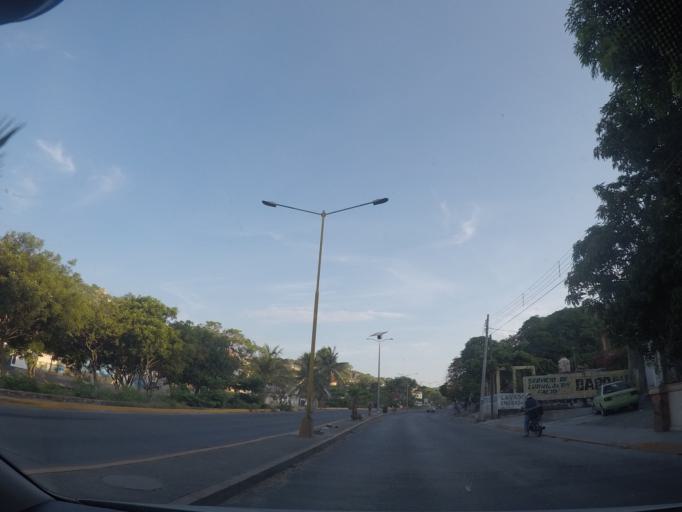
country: MX
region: Oaxaca
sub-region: Salina Cruz
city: Salina Cruz
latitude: 16.1880
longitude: -95.2013
